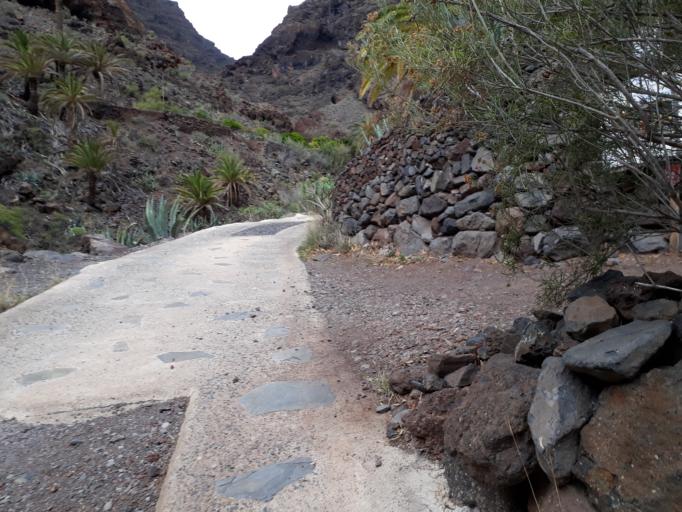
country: ES
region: Canary Islands
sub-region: Provincia de Santa Cruz de Tenerife
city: Alajero
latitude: 28.0810
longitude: -17.3217
